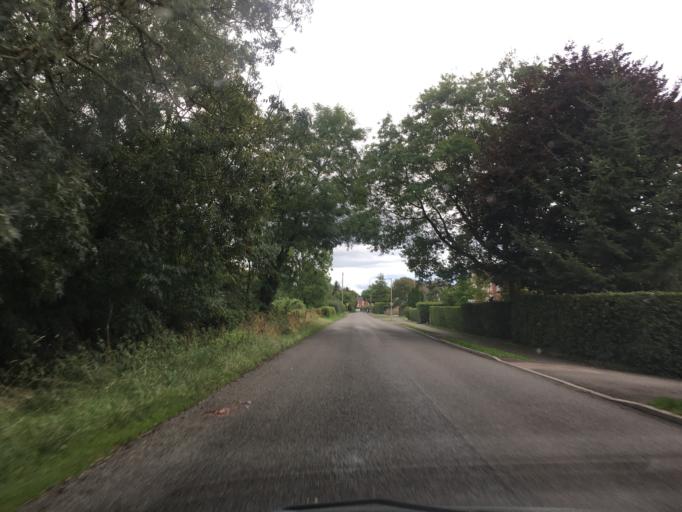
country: GB
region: England
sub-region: Leicestershire
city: Lutterworth
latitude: 52.4715
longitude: -1.2108
